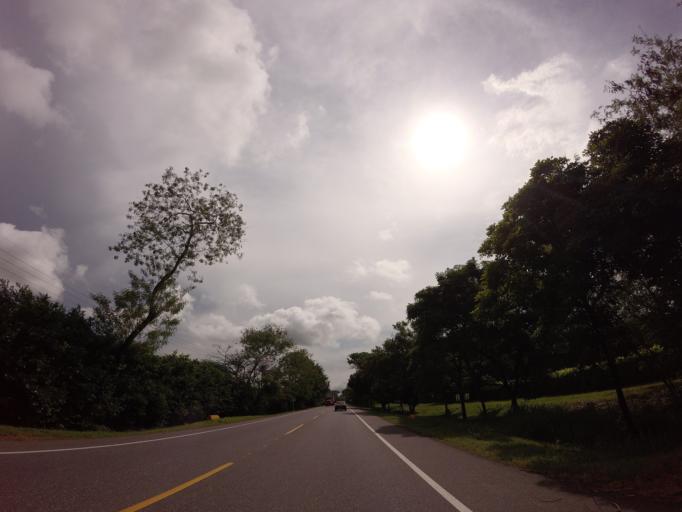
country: CO
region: Caldas
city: La Dorada
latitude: 5.3567
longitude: -74.7266
